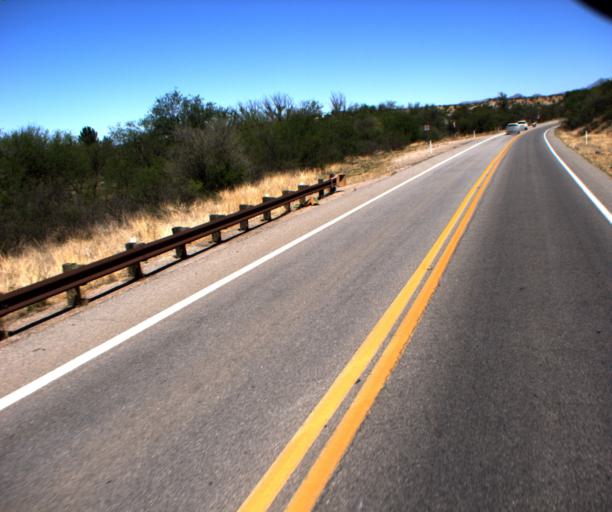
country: US
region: Arizona
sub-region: Santa Cruz County
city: Nogales
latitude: 31.3924
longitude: -110.8705
